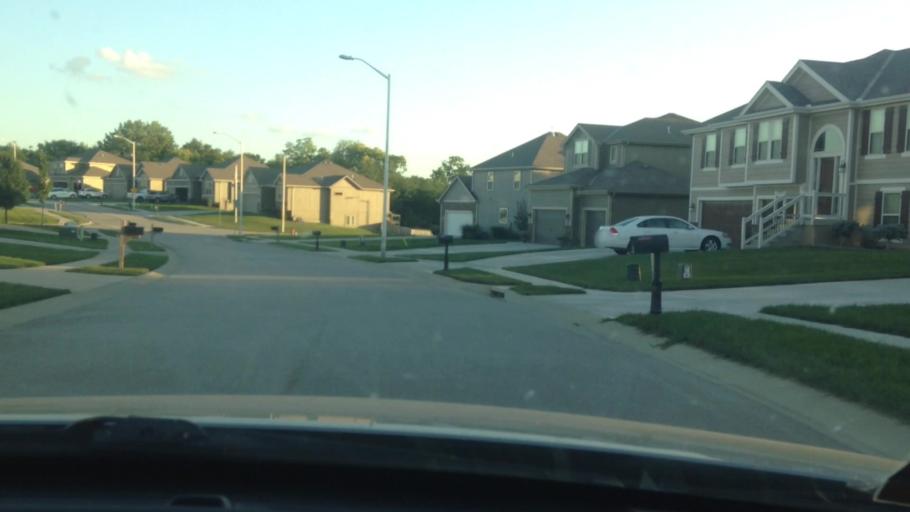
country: US
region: Missouri
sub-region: Clay County
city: Smithville
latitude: 39.2957
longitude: -94.5888
